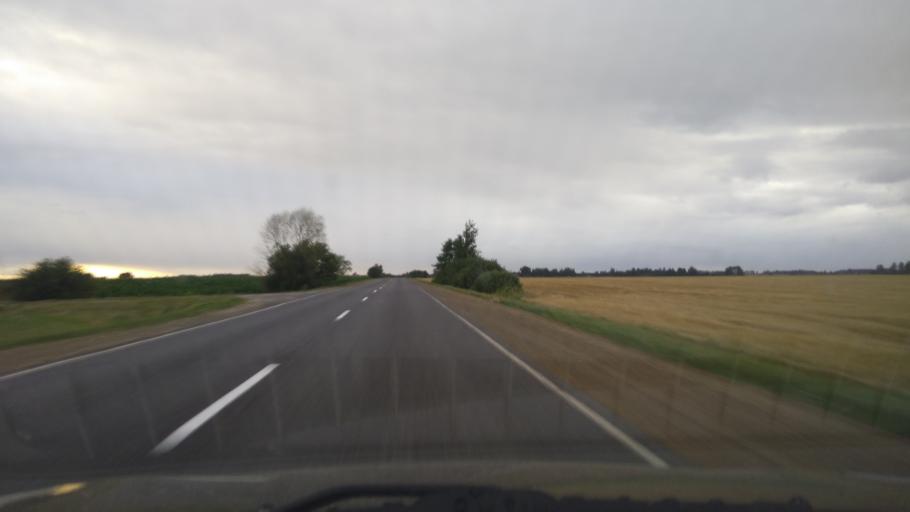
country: BY
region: Brest
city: Byaroza
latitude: 52.4396
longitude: 24.9771
